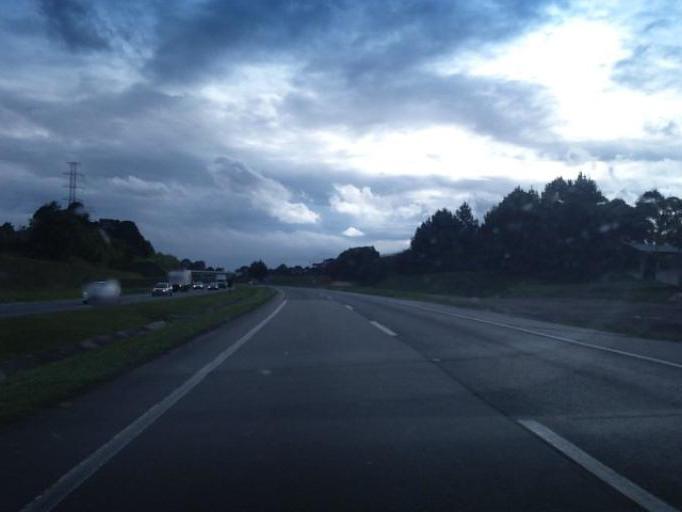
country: BR
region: Parana
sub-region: Piraquara
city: Piraquara
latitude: -25.4823
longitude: -49.1058
